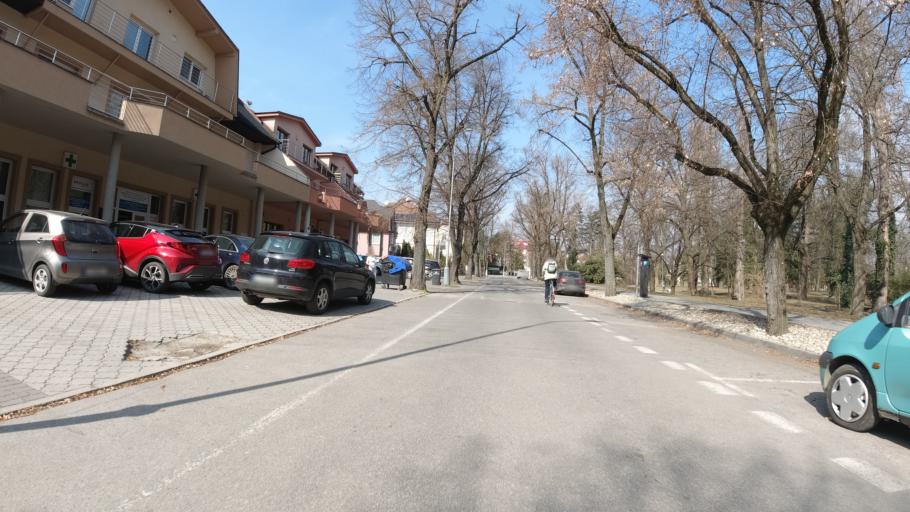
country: SK
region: Trnavsky
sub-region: Okres Trnava
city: Piestany
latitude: 48.5939
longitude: 17.8342
